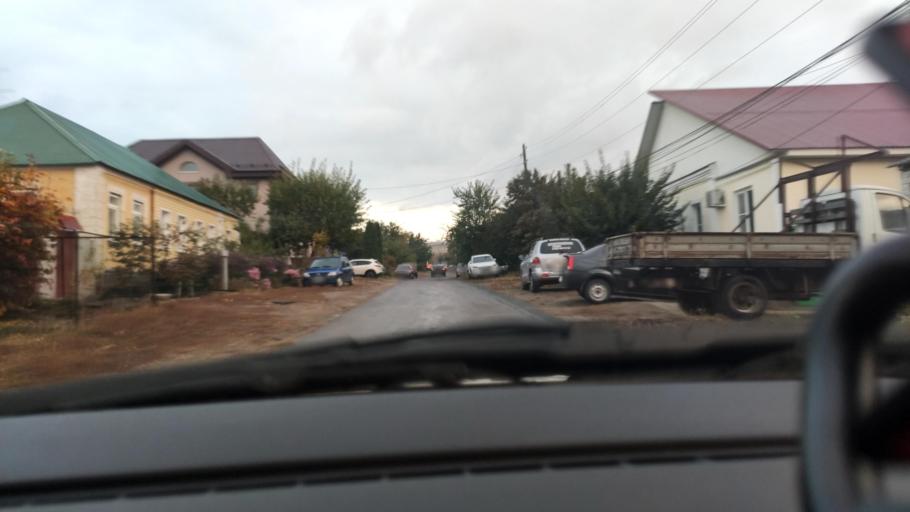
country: RU
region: Voronezj
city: Voronezh
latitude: 51.6924
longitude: 39.1562
